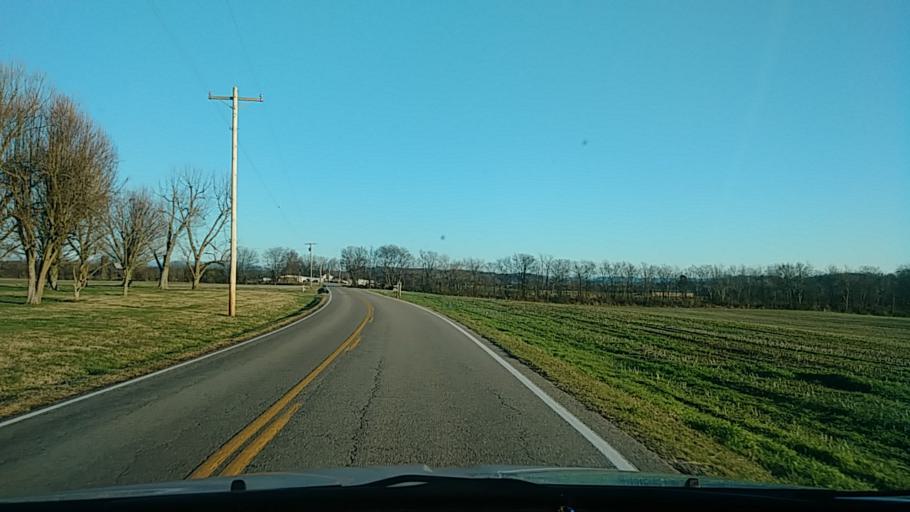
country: US
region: Tennessee
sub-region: Jefferson County
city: White Pine
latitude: 36.1518
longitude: -83.1567
